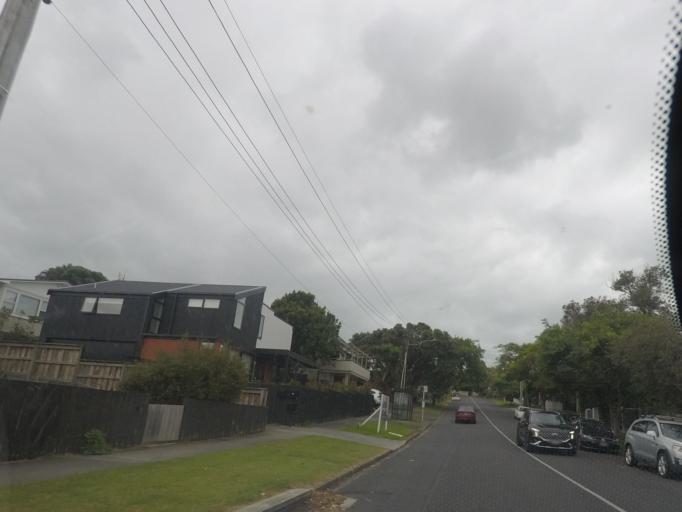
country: NZ
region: Auckland
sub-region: Auckland
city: Tamaki
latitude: -36.8650
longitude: 174.8579
